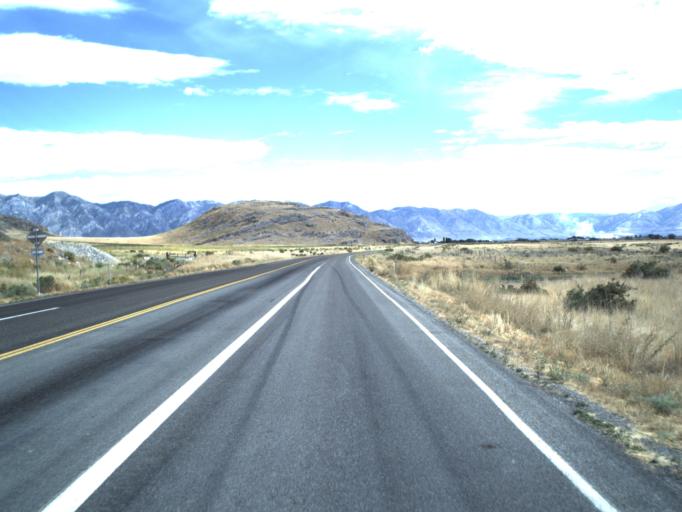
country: US
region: Utah
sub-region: Box Elder County
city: Elwood
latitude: 41.5790
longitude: -112.2482
